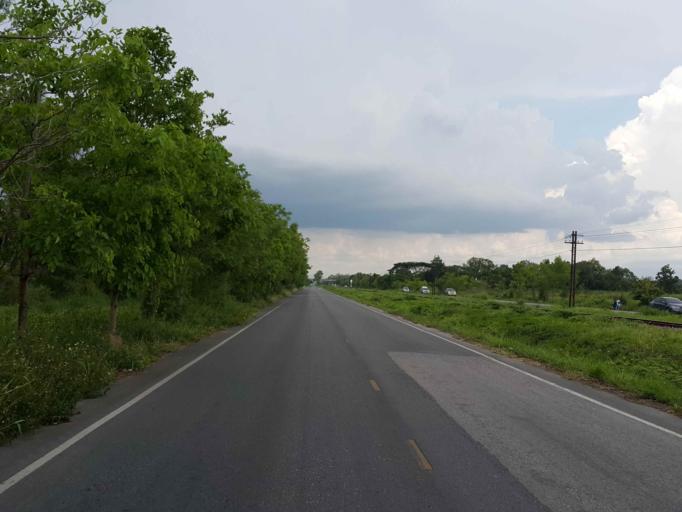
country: TH
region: Chiang Mai
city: Saraphi
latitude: 18.7423
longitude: 99.0281
